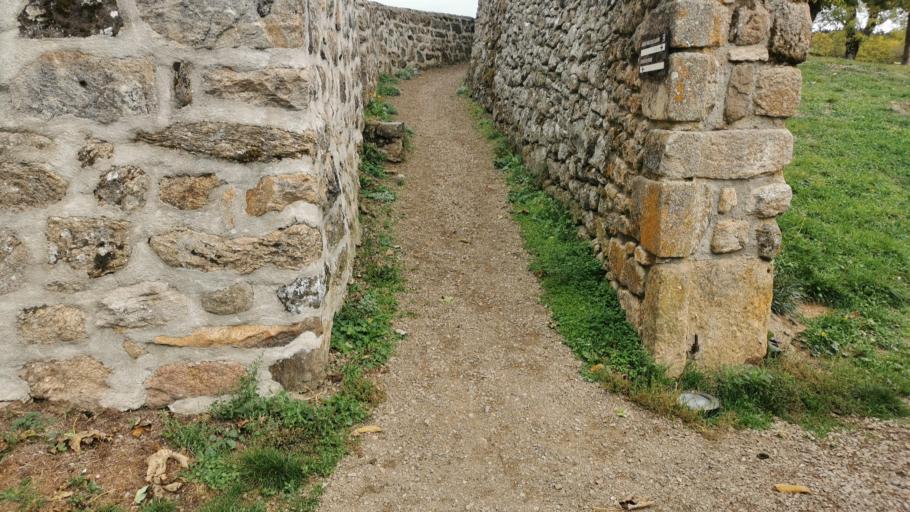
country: FR
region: Languedoc-Roussillon
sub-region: Departement de la Lozere
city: Langogne
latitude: 44.7684
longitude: 3.8832
